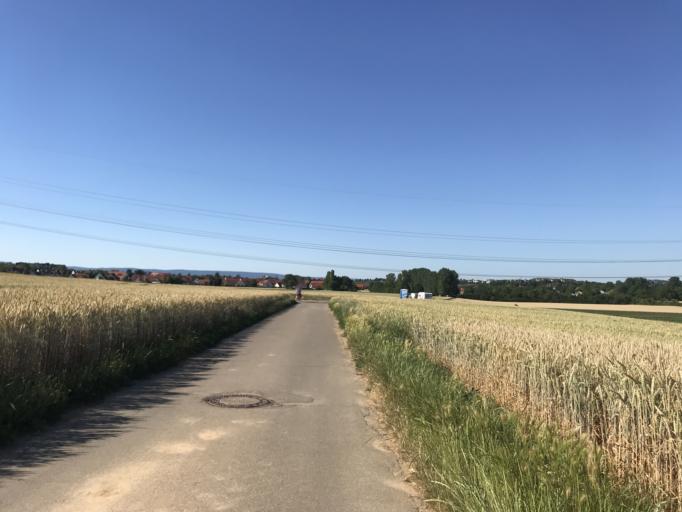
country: DE
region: Rheinland-Pfalz
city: Gau-Bischofsheim
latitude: 49.9494
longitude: 8.2745
